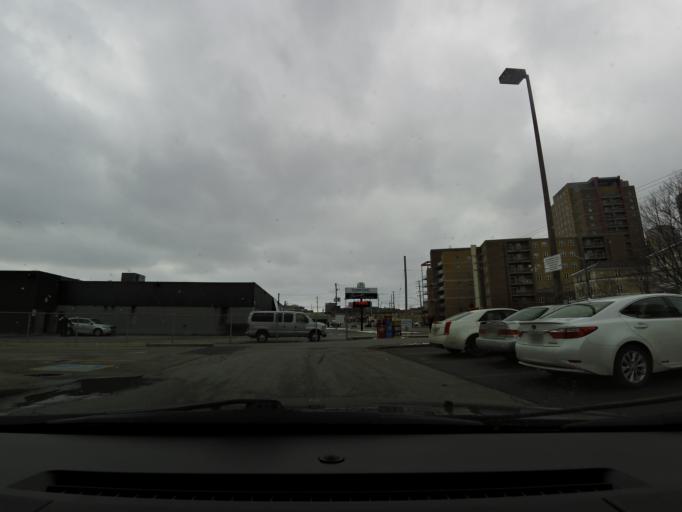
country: CA
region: Ontario
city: Waterloo
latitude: 43.4772
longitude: -80.5216
